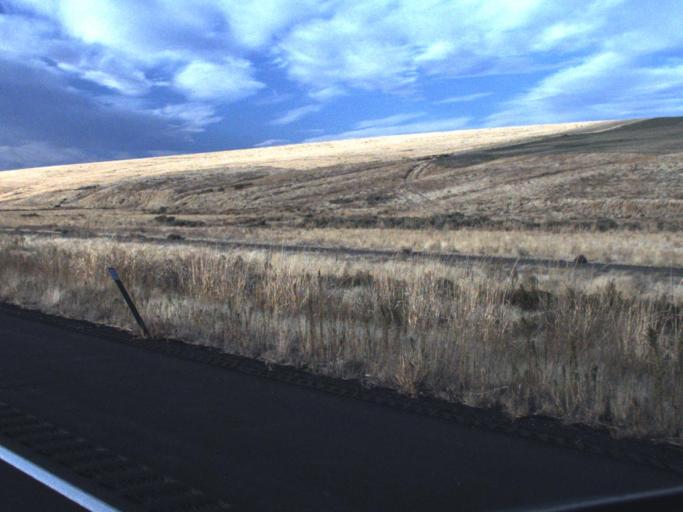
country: US
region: Washington
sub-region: Franklin County
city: Connell
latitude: 46.8535
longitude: -118.6384
